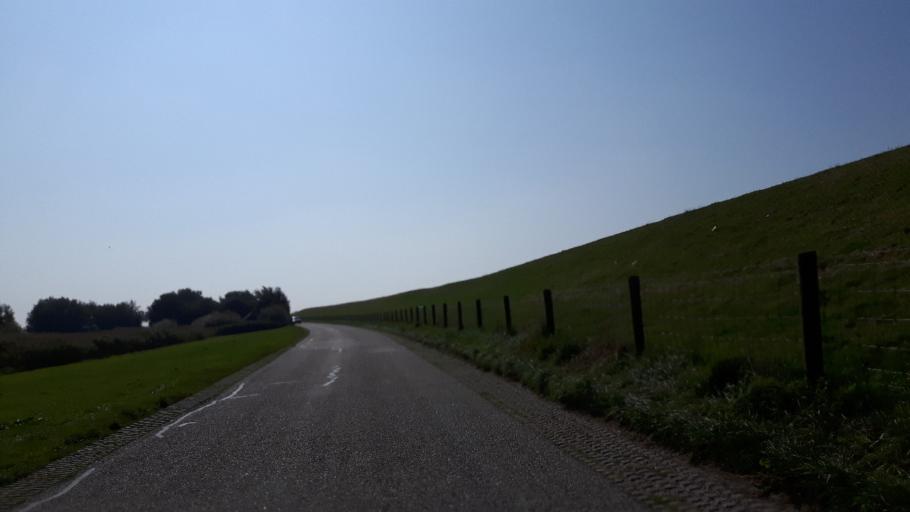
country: NL
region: Friesland
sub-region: Sudwest Fryslan
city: Makkum
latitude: 53.0855
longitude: 5.3830
